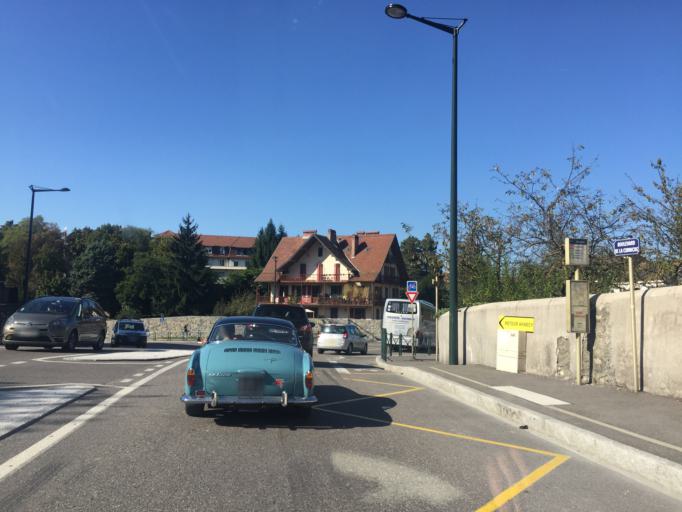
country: FR
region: Rhone-Alpes
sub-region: Departement de la Haute-Savoie
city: Annecy
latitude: 45.8947
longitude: 6.1278
